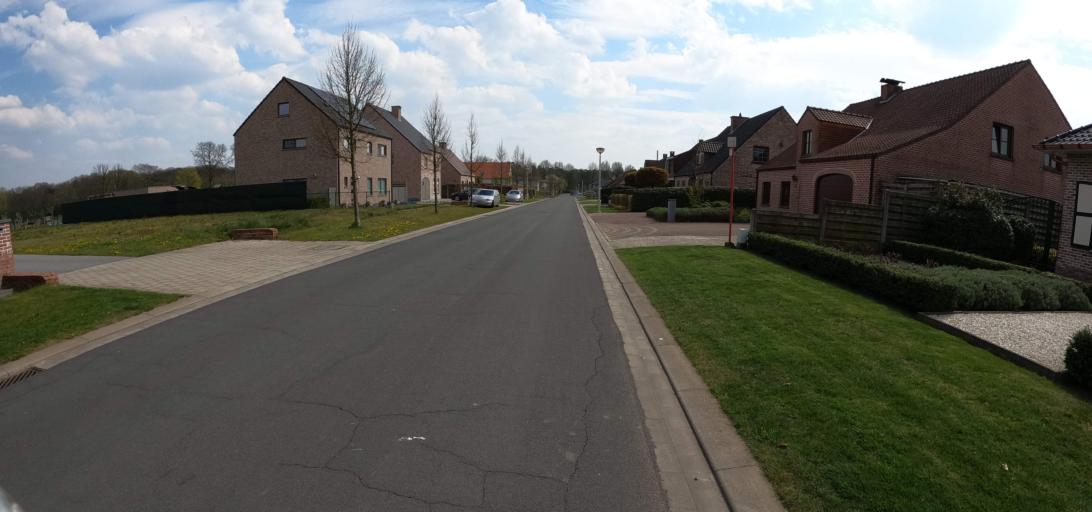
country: BE
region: Flanders
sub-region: Provincie Antwerpen
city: Oostmalle
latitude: 51.3107
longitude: 4.7477
